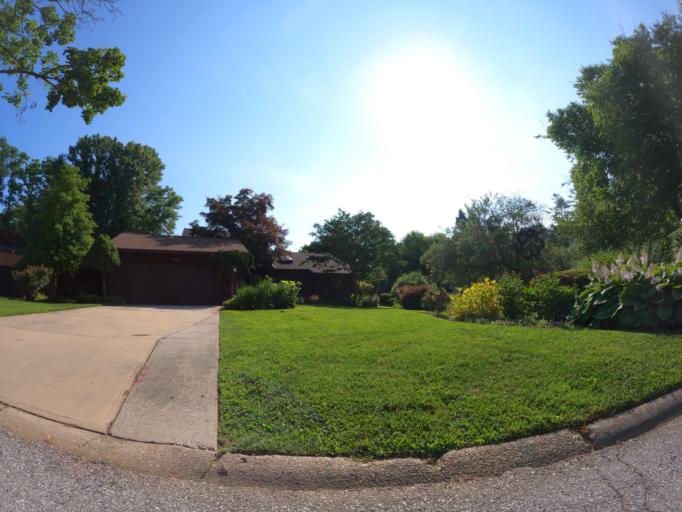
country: US
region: Maryland
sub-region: Howard County
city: Columbia
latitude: 39.2267
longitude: -76.8608
